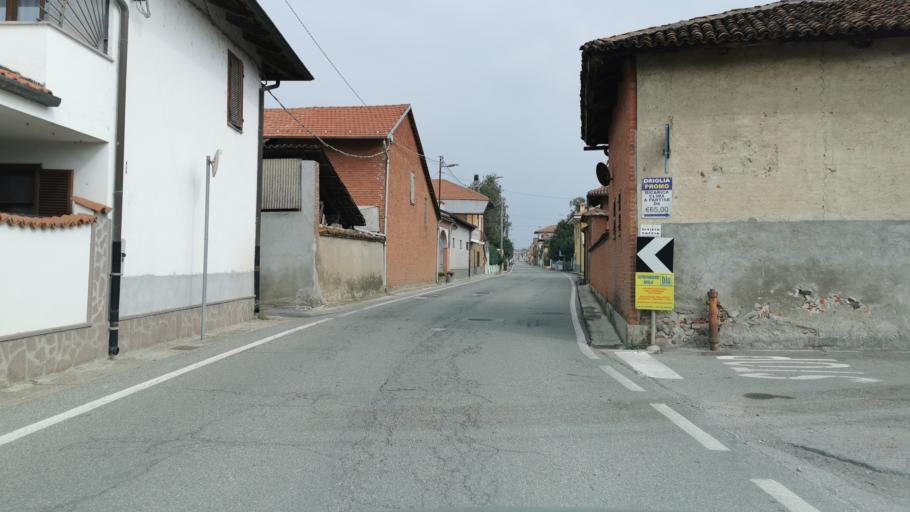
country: IT
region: Piedmont
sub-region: Provincia di Torino
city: Tonengo-Casale
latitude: 45.2790
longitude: 7.9339
